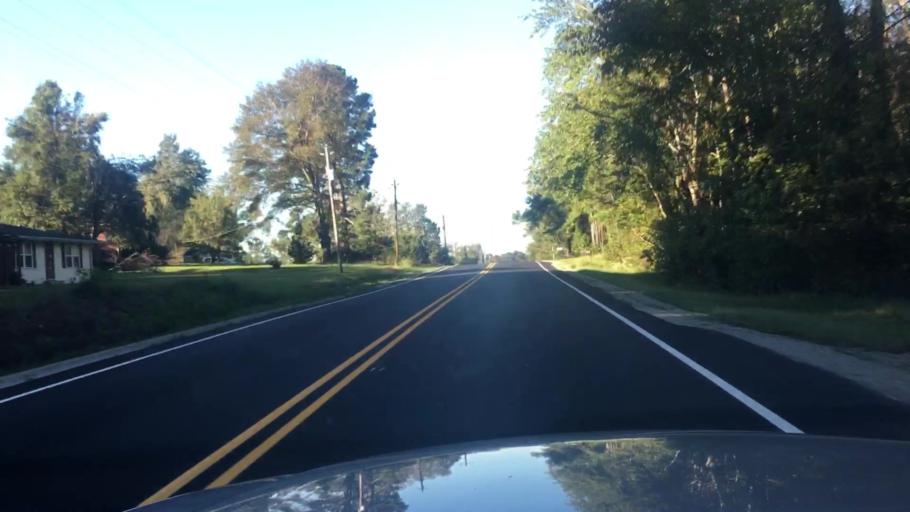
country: US
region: North Carolina
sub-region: Harnett County
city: Walkertown
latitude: 35.3169
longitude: -78.8793
